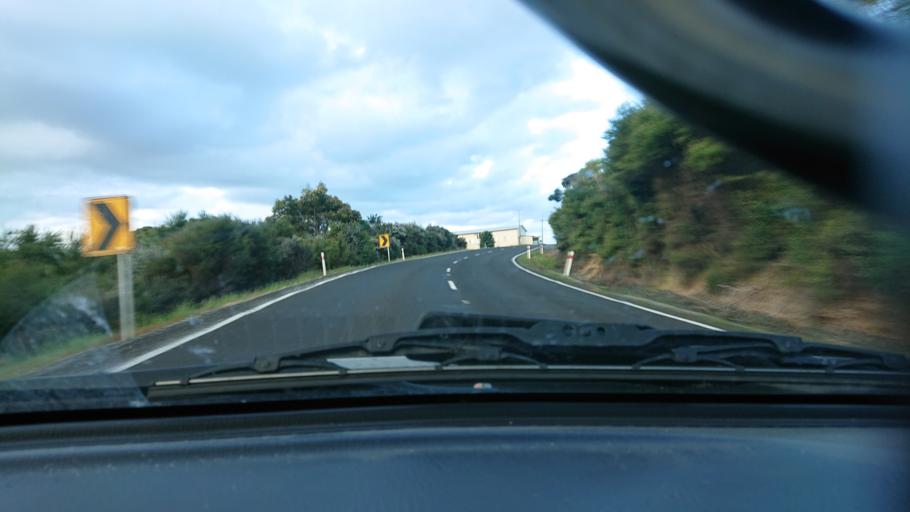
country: NZ
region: Auckland
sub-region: Auckland
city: Parakai
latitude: -36.4756
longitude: 174.4477
